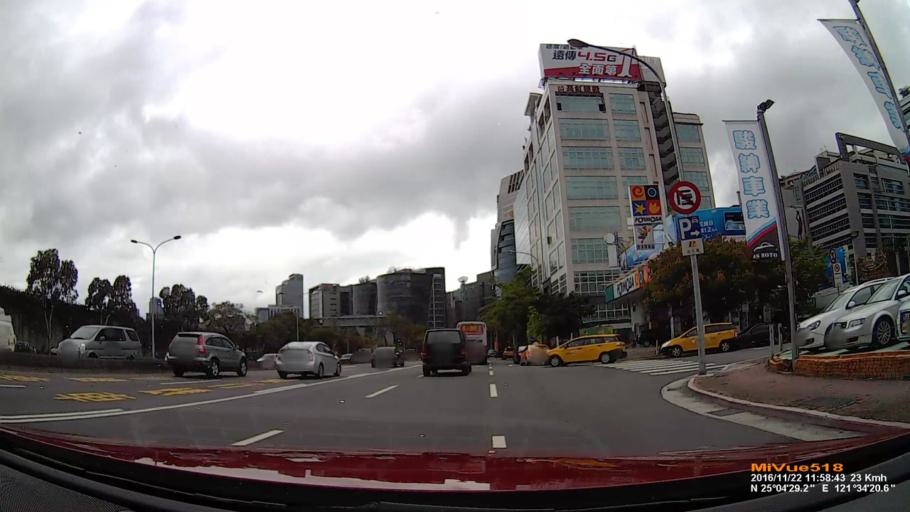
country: TW
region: Taipei
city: Taipei
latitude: 25.0749
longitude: 121.5723
